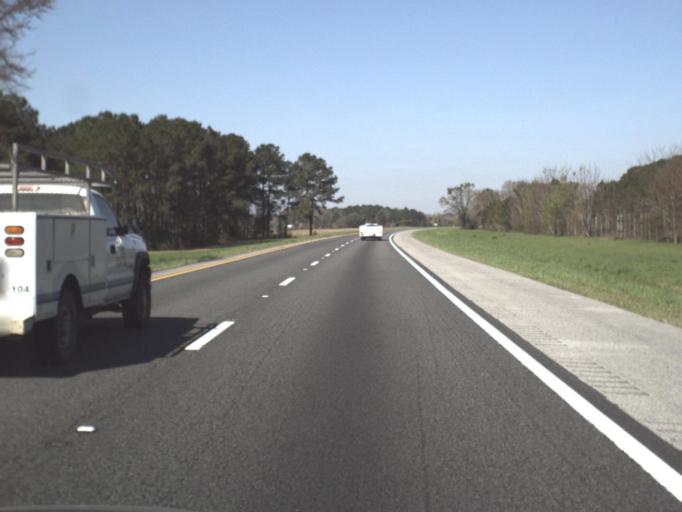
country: US
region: Florida
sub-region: Jackson County
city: Sneads
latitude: 30.6406
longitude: -84.9965
